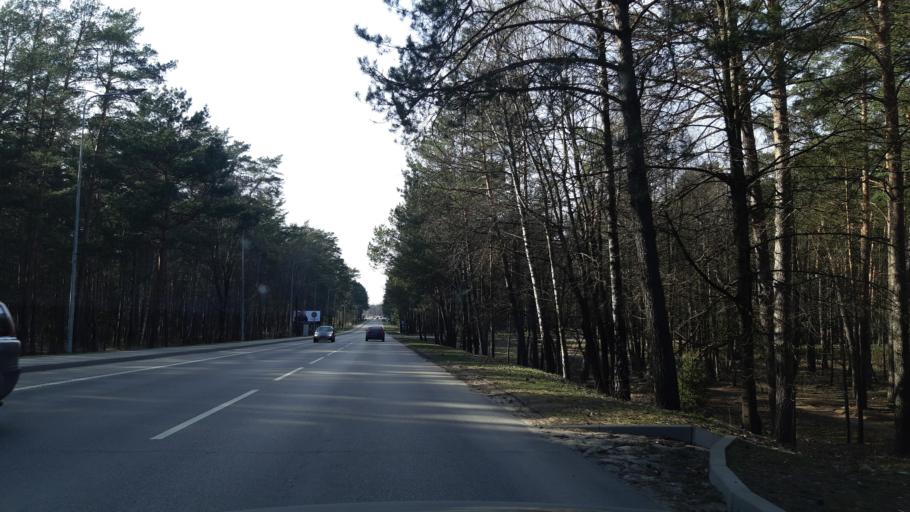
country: LT
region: Alytaus apskritis
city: Druskininkai
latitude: 54.0068
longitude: 24.0025
